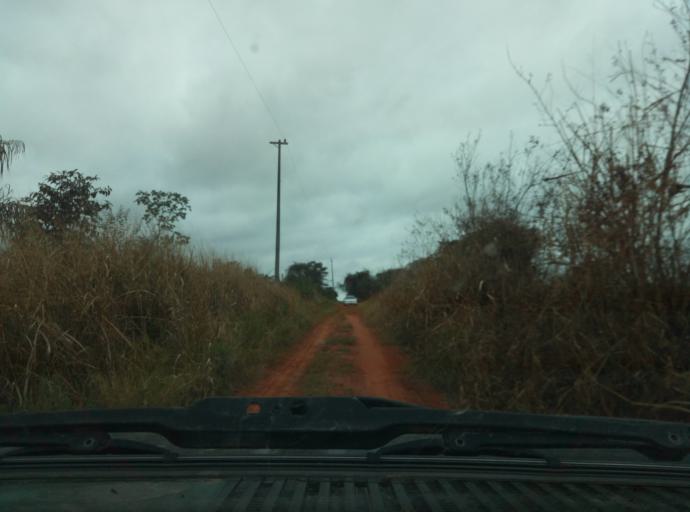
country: PY
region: Caaguazu
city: Doctor Cecilio Baez
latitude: -25.1609
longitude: -56.2719
